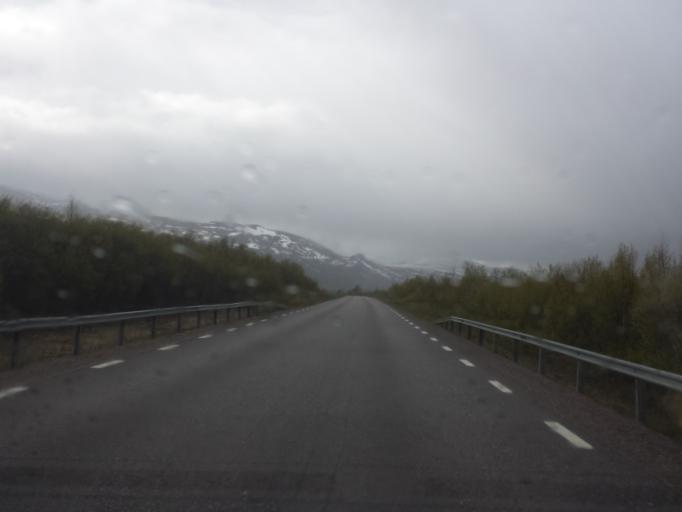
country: SE
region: Norrbotten
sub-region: Kiruna Kommun
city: Kiruna
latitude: 68.2328
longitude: 19.6085
